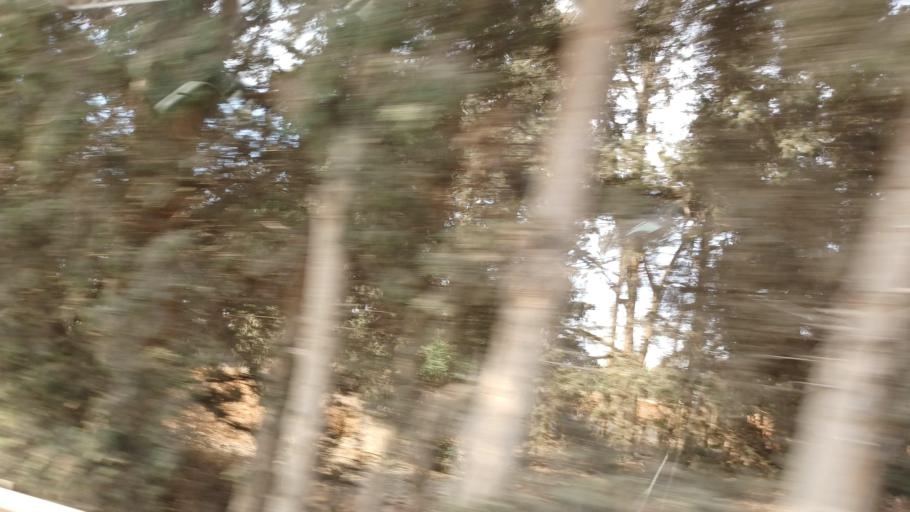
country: CY
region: Ammochostos
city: Frenaros
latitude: 35.0522
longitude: 33.9385
